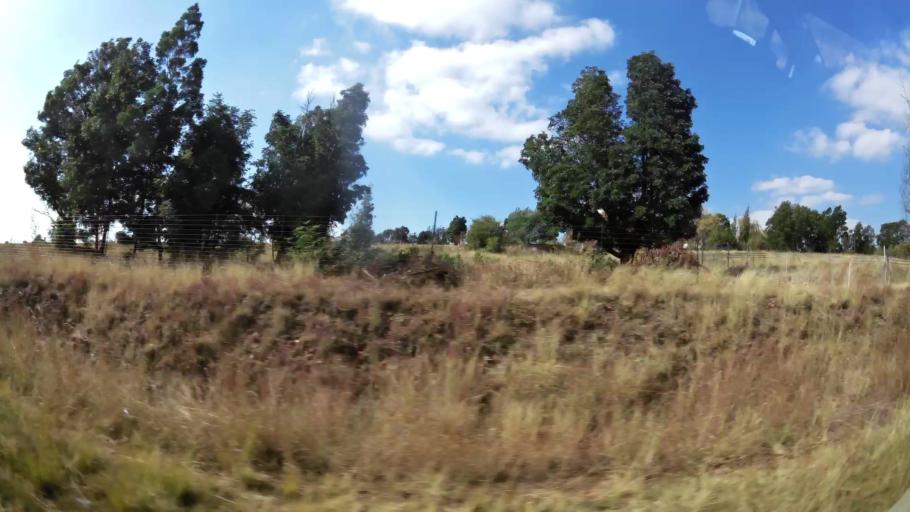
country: ZA
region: Gauteng
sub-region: West Rand District Municipality
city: Krugersdorp
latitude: -26.0395
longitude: 27.7423
